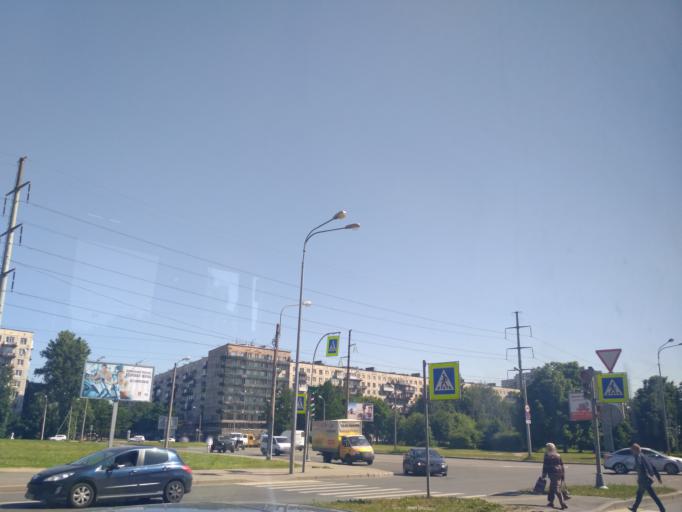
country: RU
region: Leningrad
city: Kalininskiy
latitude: 59.9766
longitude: 30.4016
